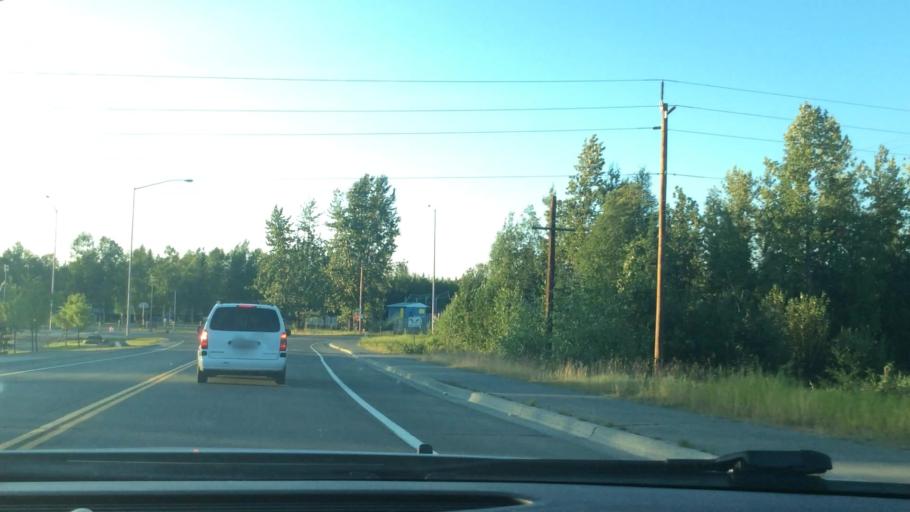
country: US
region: Alaska
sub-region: Anchorage Municipality
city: Anchorage
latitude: 61.2252
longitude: -149.7917
